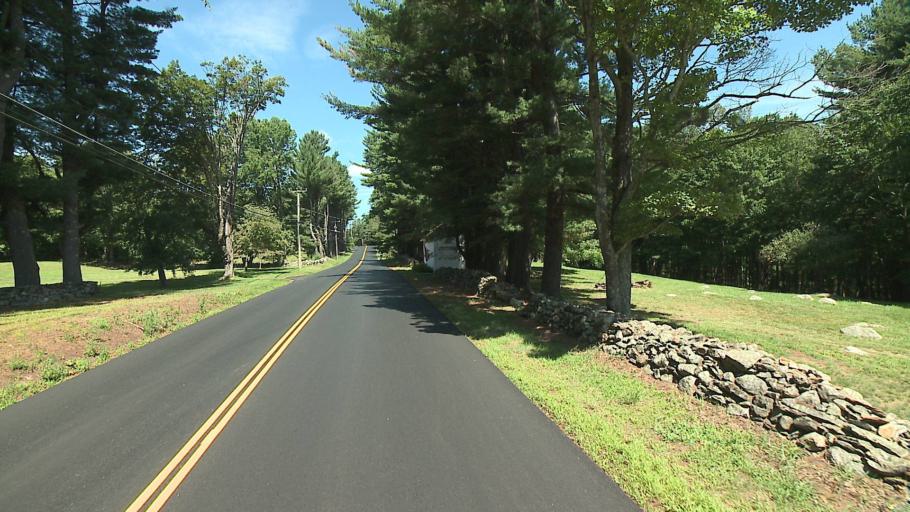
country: US
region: Connecticut
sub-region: Hartford County
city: West Simsbury
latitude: 41.9133
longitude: -72.9013
